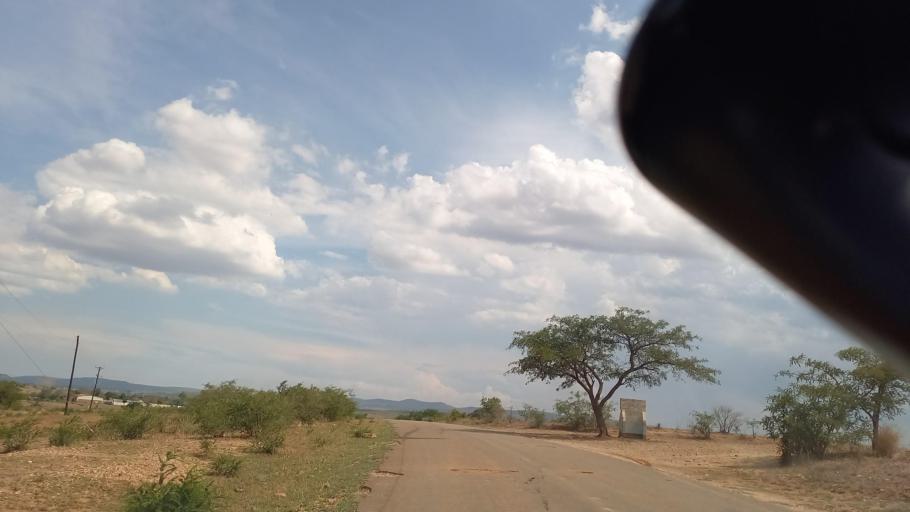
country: ZM
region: Lusaka
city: Kafue
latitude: -16.1859
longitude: 28.0871
